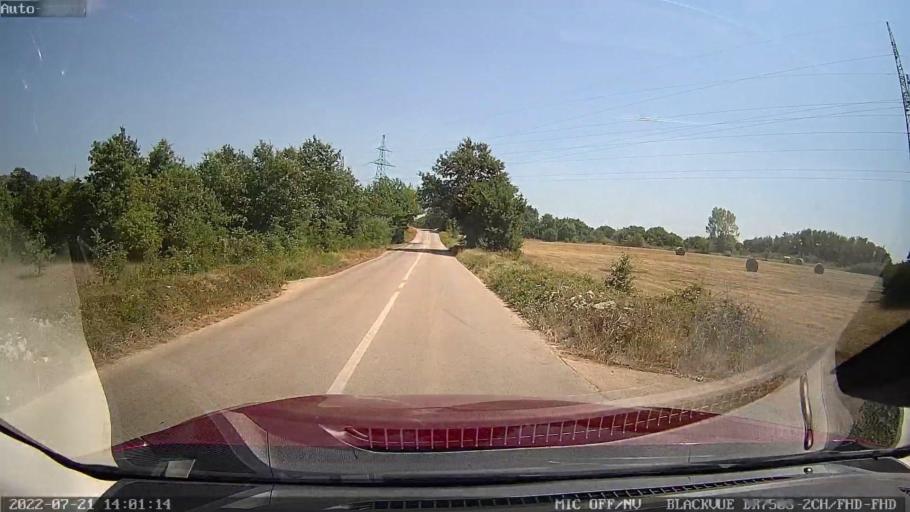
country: HR
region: Istarska
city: Vodnjan
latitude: 45.0945
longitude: 13.8779
